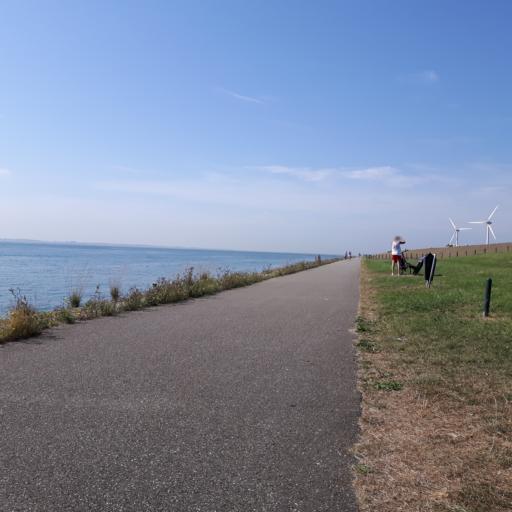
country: NL
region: Zeeland
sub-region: Gemeente Vlissingen
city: Vlissingen
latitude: 51.4417
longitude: 3.6177
